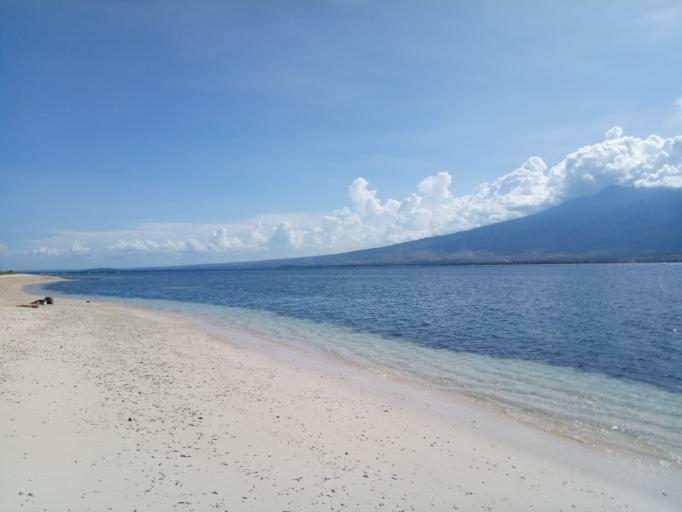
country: ID
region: West Nusa Tenggara
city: Sambelia
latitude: -8.4431
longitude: 116.7325
